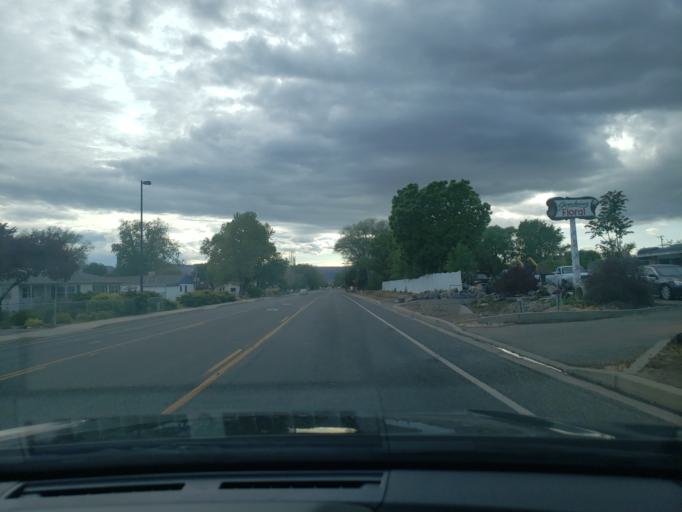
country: US
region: Colorado
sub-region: Mesa County
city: Orchard Mesa
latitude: 39.0484
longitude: -108.5324
